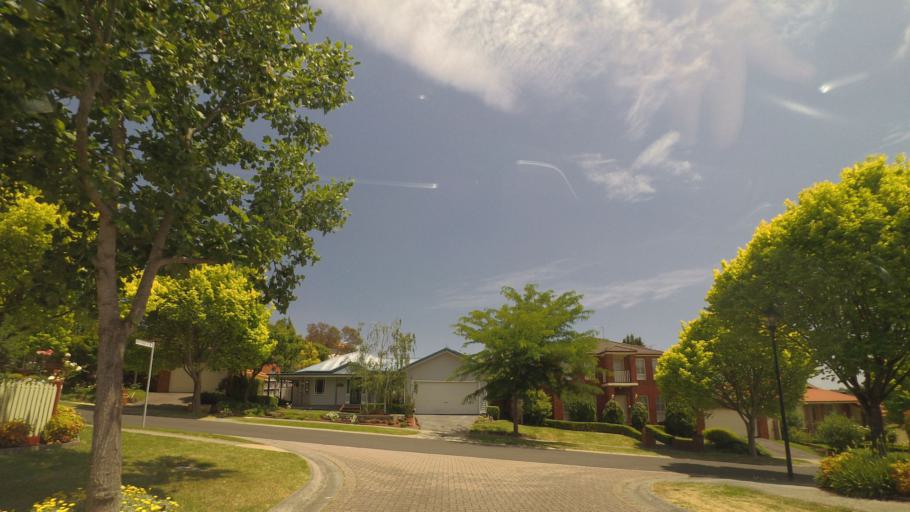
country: AU
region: Victoria
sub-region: Yarra Ranges
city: Chirnside Park
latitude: -37.7582
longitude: 145.3024
